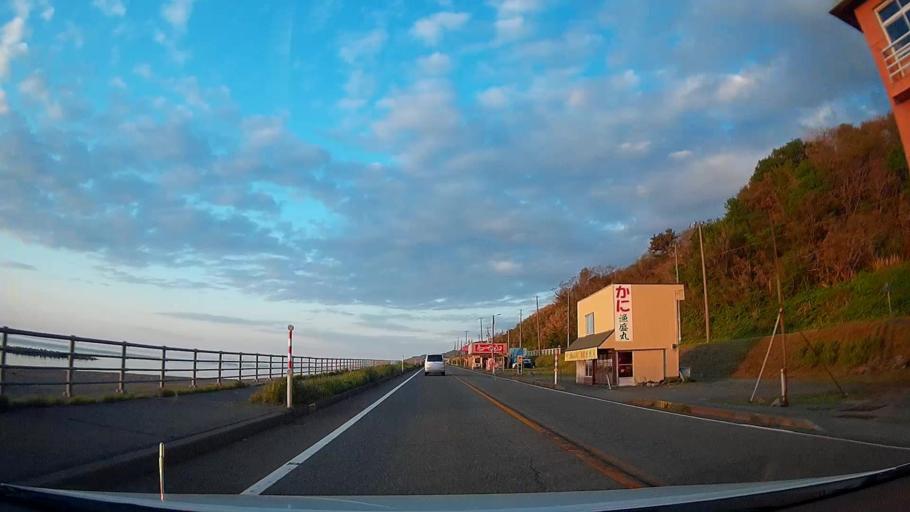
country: JP
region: Niigata
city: Itoigawa
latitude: 37.1163
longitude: 138.0277
